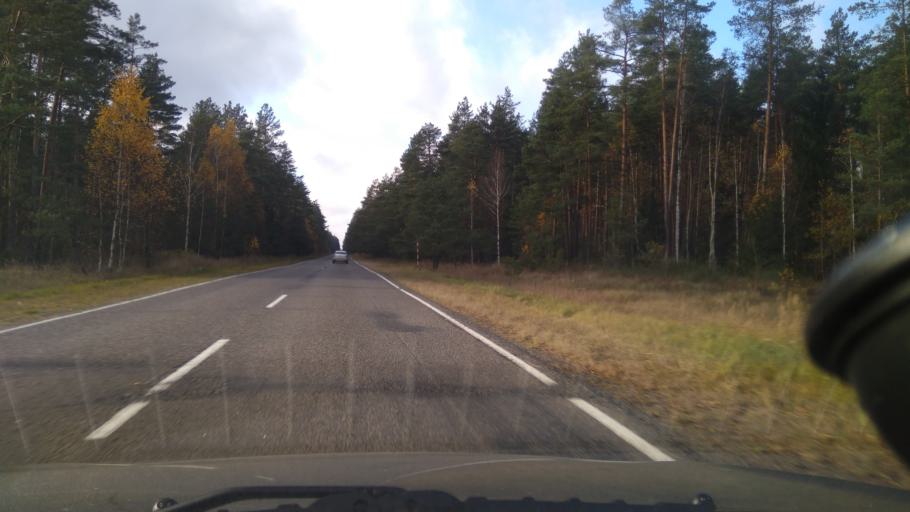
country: BY
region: Minsk
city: Slutsk
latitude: 53.2297
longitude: 27.7007
